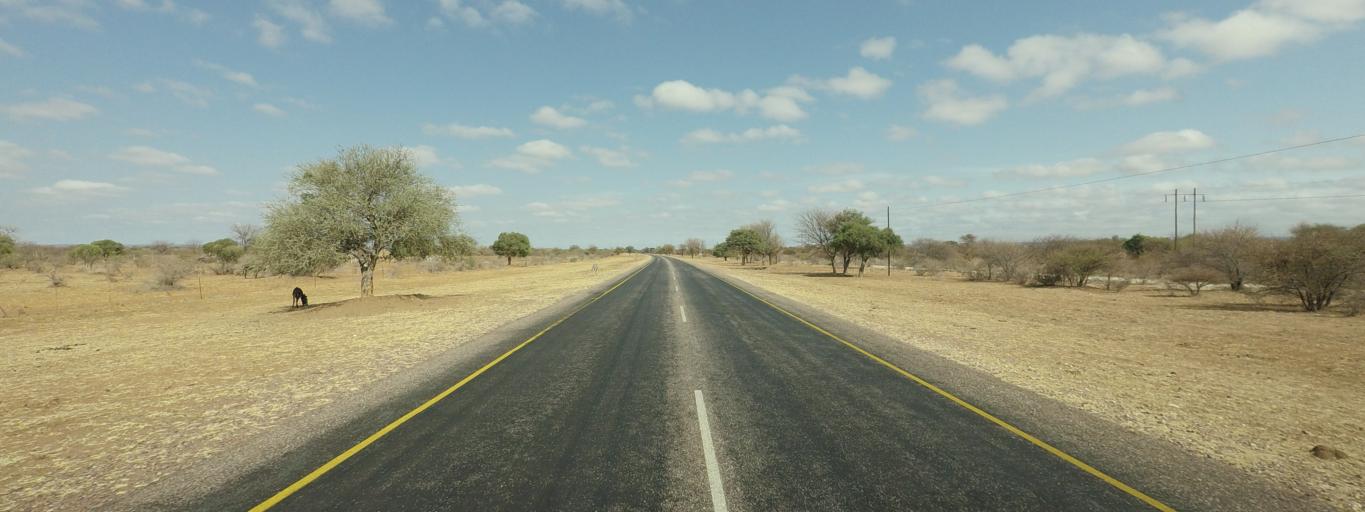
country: BW
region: Central
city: Ratholo
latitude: -22.8053
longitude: 27.5209
